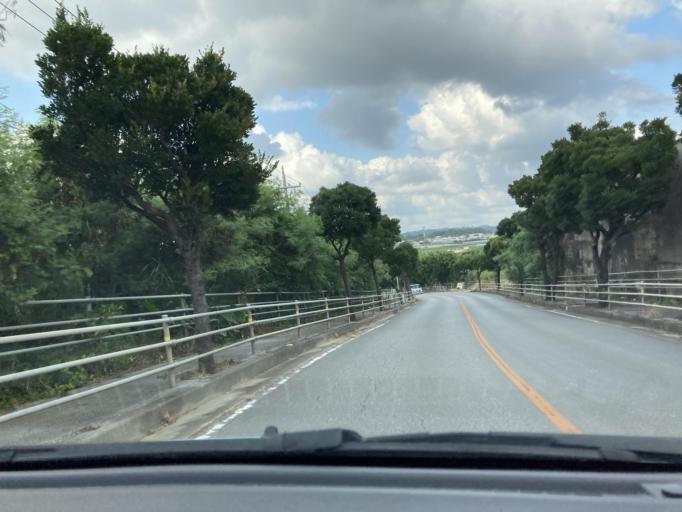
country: JP
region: Okinawa
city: Itoman
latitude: 26.0952
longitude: 127.6646
